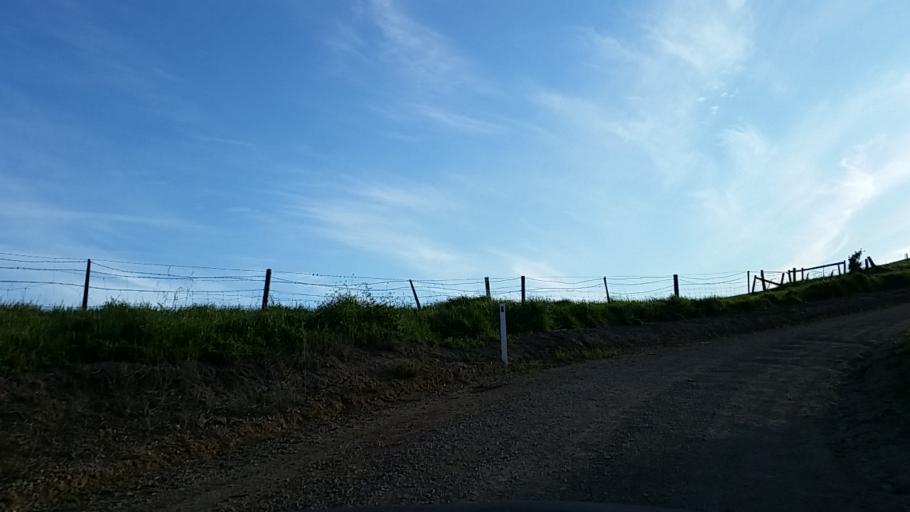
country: AU
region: South Australia
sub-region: Mount Barker
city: Meadows
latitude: -35.2421
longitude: 138.7613
